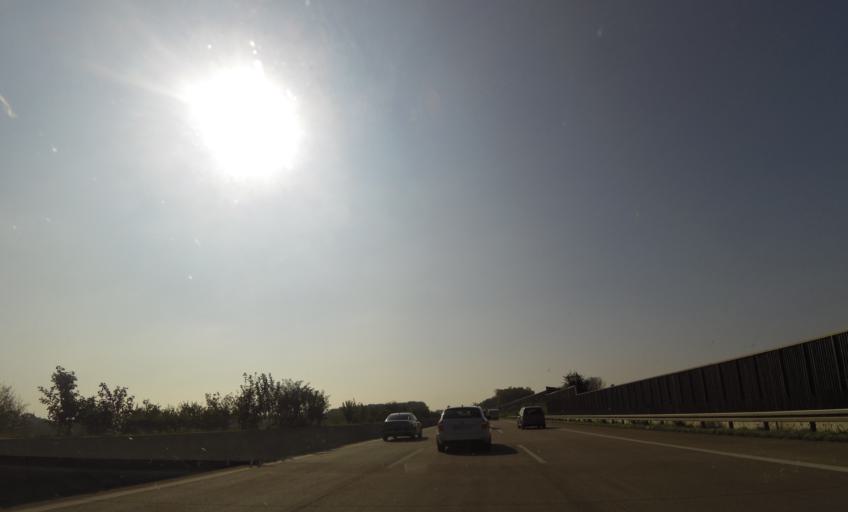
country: DE
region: Baden-Wuerttemberg
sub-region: Karlsruhe Region
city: Zell
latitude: 48.6657
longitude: 8.0440
